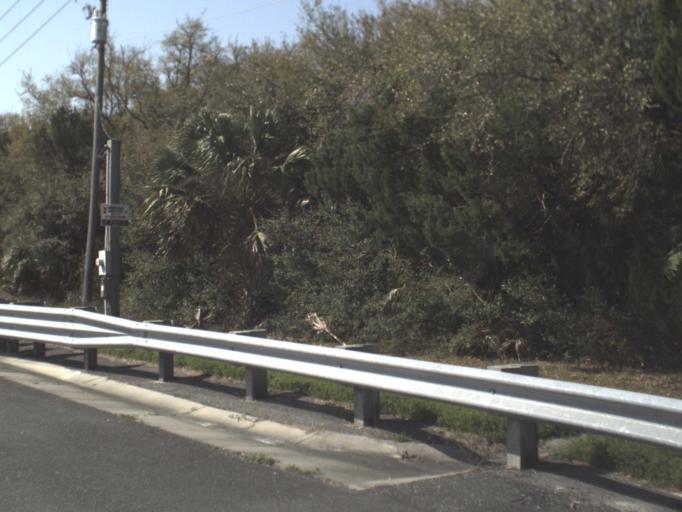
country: US
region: Florida
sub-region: Franklin County
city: Eastpoint
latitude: 29.7249
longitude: -84.8880
